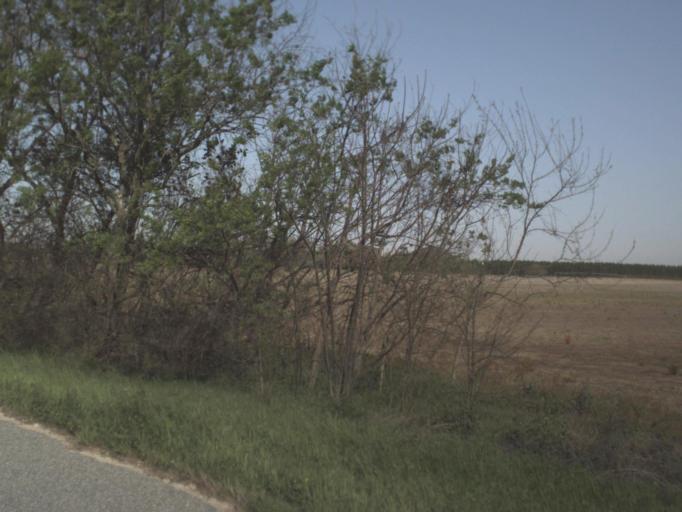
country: US
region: Florida
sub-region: Jackson County
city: Malone
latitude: 30.9755
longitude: -85.0802
